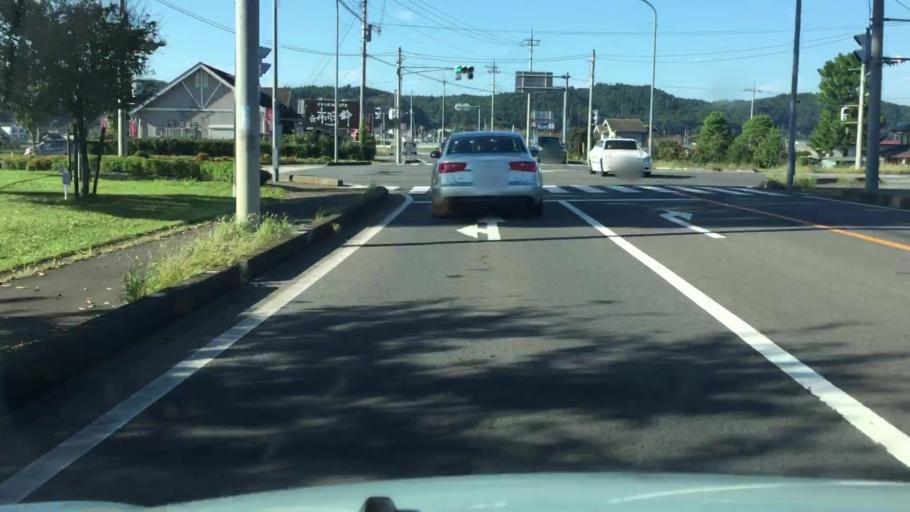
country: JP
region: Tochigi
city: Ujiie
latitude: 36.7161
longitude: 140.0316
